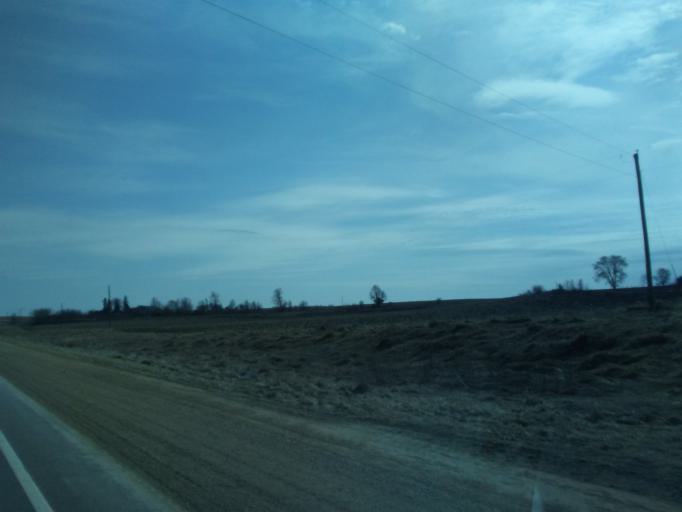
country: US
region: Iowa
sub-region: Winneshiek County
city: Decorah
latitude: 43.3887
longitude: -91.8288
